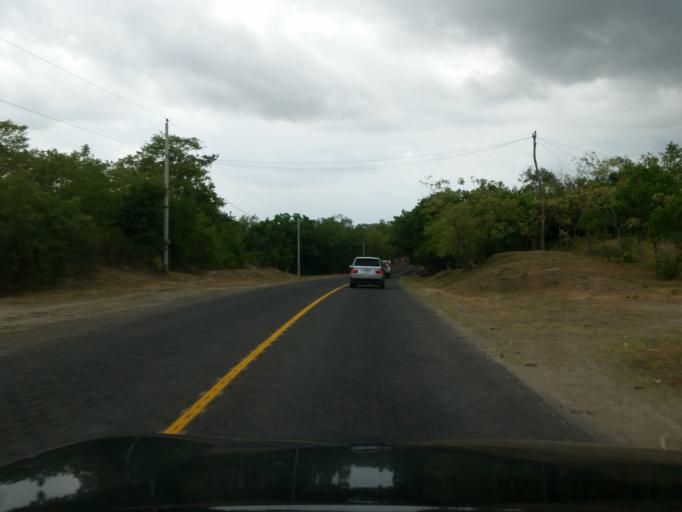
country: NI
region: Managua
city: Carlos Fonseca Amador
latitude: 11.9298
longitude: -86.5065
